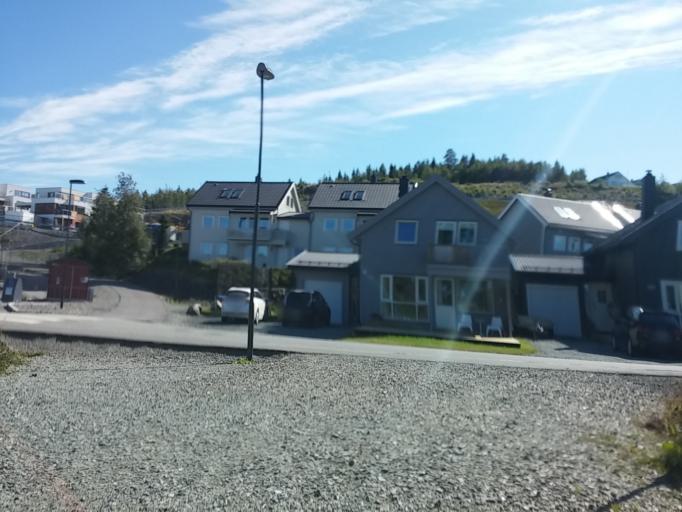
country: NO
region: Sor-Trondelag
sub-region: Malvik
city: Hommelvik
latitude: 63.4294
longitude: 10.7542
